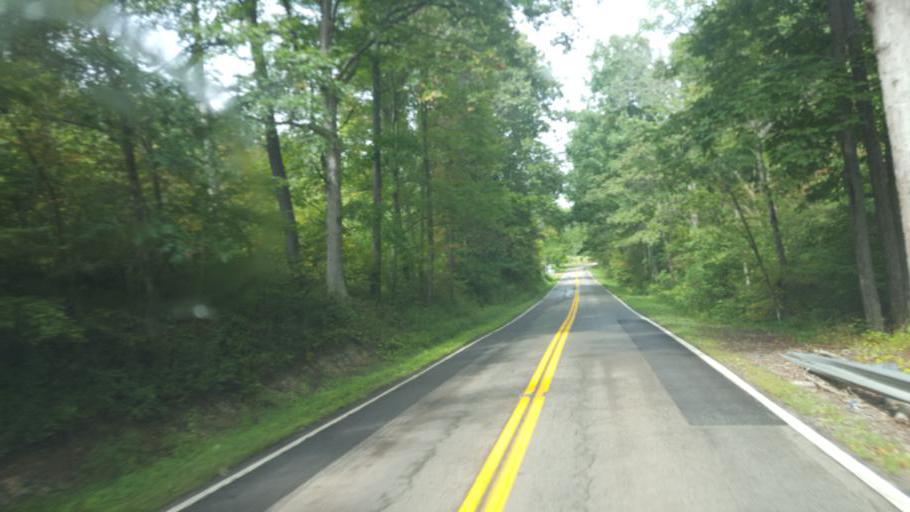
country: US
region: Ohio
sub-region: Jackson County
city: Oak Hill
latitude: 38.8843
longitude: -82.6631
